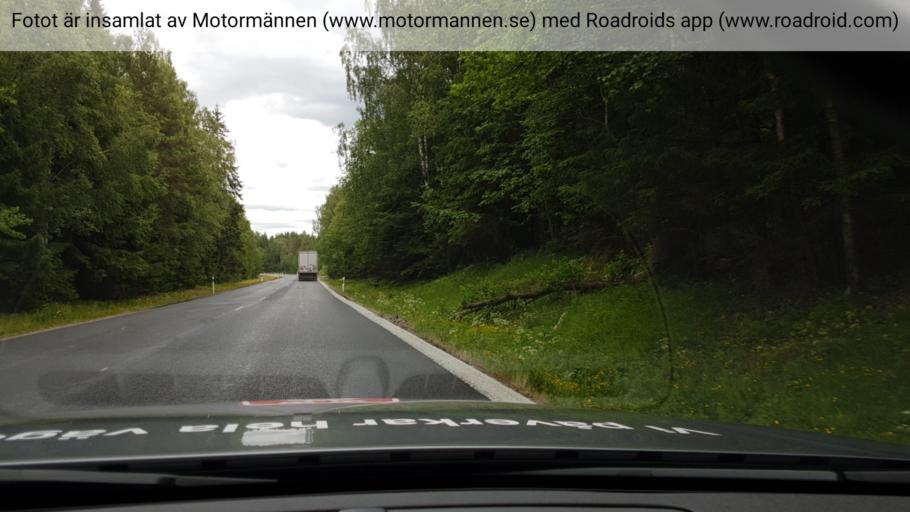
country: SE
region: Vaestmanland
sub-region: Skinnskattebergs Kommun
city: Skinnskatteberg
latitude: 59.8706
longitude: 15.6282
